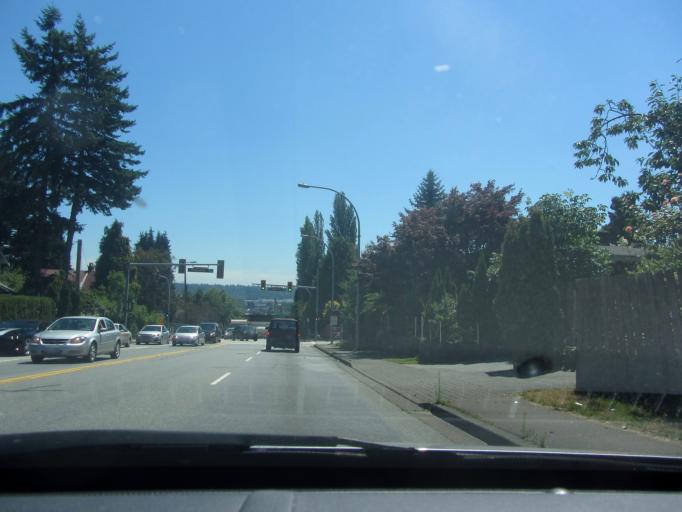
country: CA
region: British Columbia
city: New Westminster
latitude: 49.2020
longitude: -122.9474
